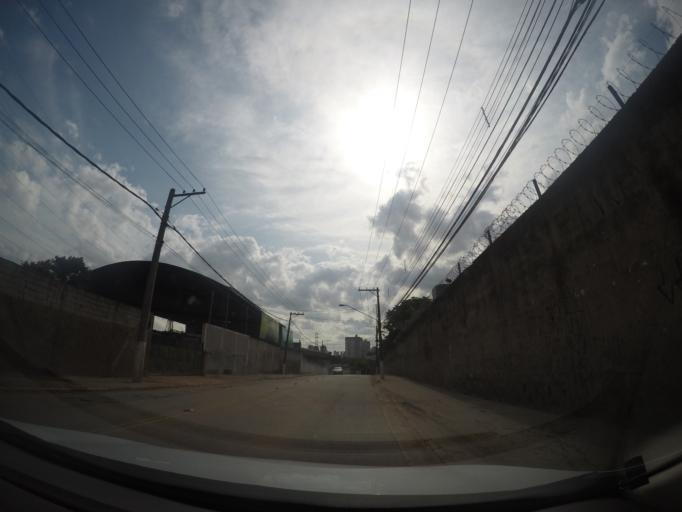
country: BR
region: Sao Paulo
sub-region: Guarulhos
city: Guarulhos
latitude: -23.4652
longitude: -46.5097
